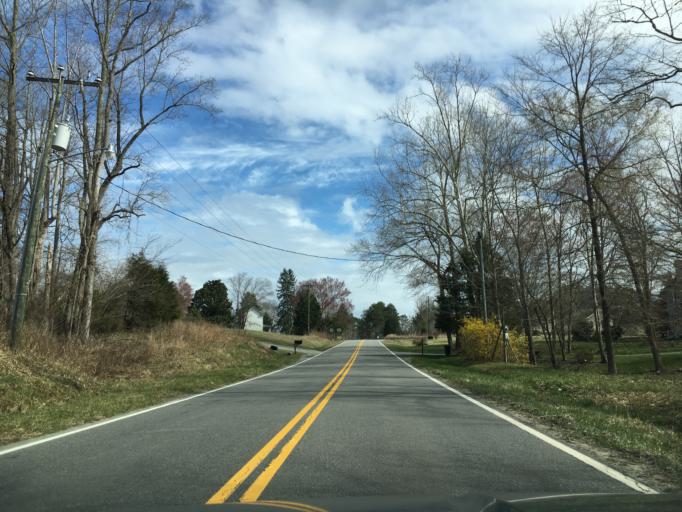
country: US
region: Virginia
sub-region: Halifax County
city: Halifax
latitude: 36.7617
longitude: -78.9117
